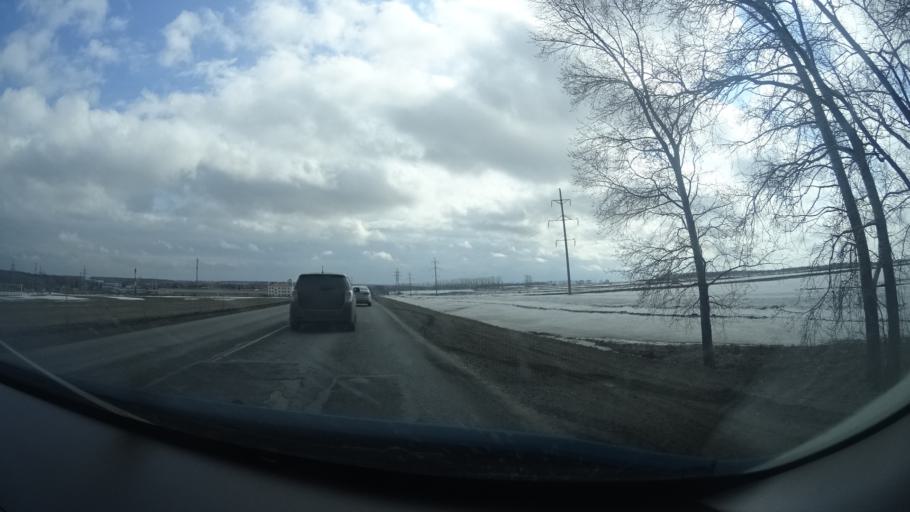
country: RU
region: Bashkortostan
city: Mikhaylovka
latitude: 54.8359
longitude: 55.8061
